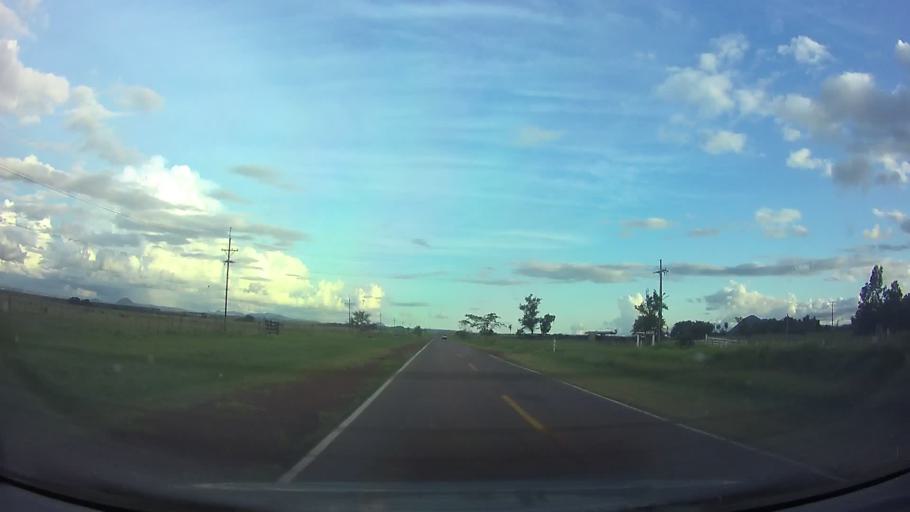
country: PY
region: Paraguari
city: Carapegua
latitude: -25.8228
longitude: -57.1670
